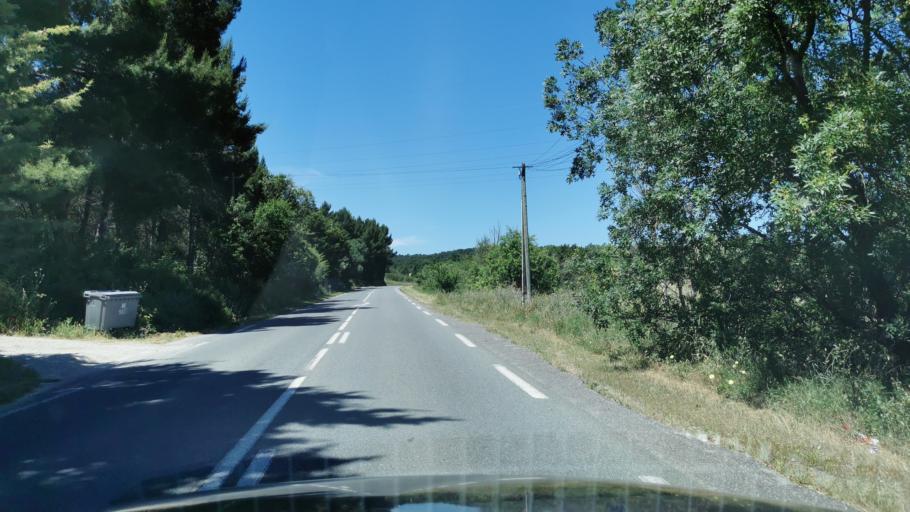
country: FR
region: Languedoc-Roussillon
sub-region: Departement de l'Aude
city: Moussan
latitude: 43.2020
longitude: 2.9666
